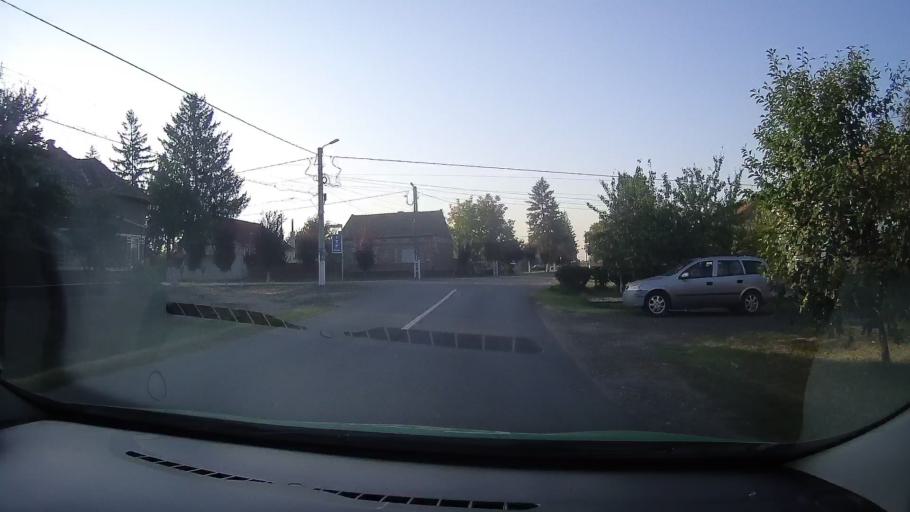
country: RO
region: Arad
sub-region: Comuna Curtici
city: Curtici
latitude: 46.3345
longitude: 21.3055
